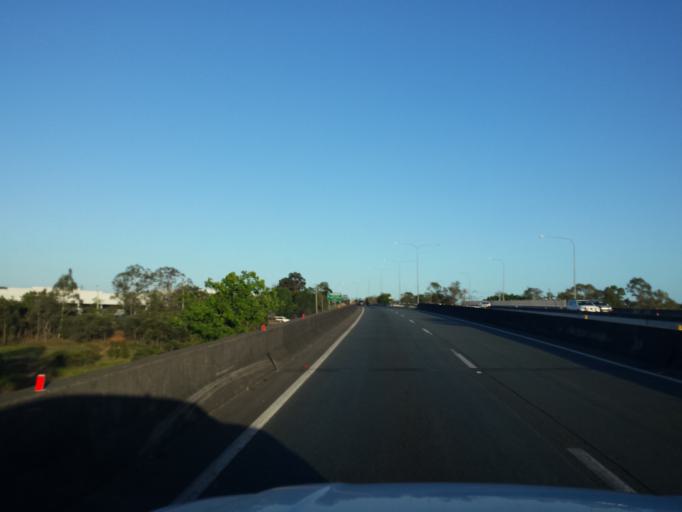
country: AU
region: Queensland
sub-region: Logan
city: Waterford West
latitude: -27.6685
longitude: 153.1195
